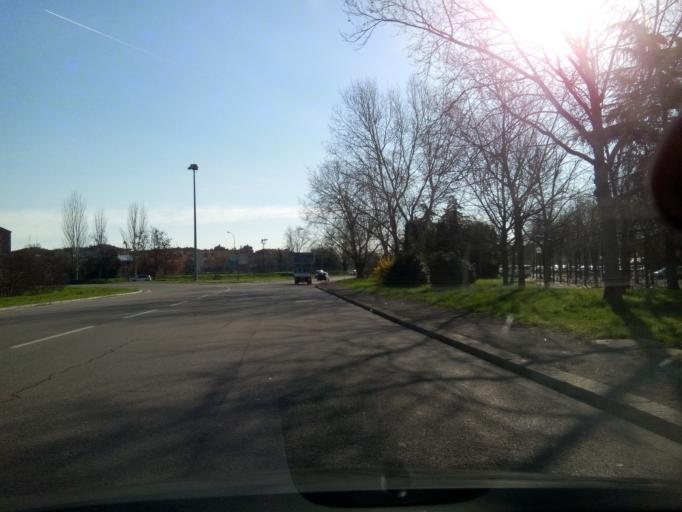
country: IT
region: Emilia-Romagna
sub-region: Provincia di Bologna
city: Bologna
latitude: 44.4996
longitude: 11.3049
